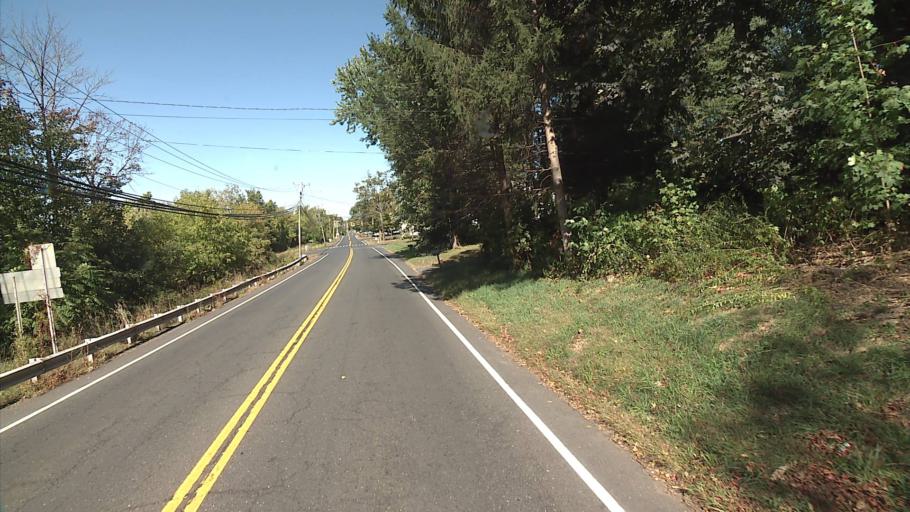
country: US
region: Connecticut
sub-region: Tolland County
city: Ellington
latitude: 41.9094
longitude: -72.4548
